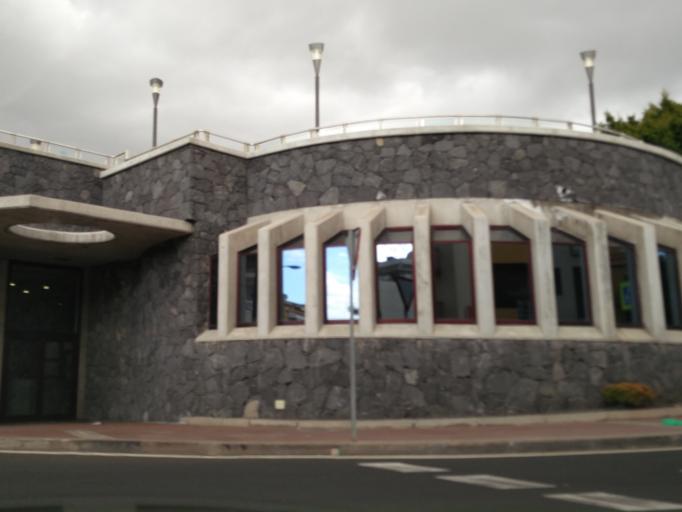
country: ES
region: Canary Islands
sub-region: Provincia de Santa Cruz de Tenerife
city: Arona
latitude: 28.0787
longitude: -16.6826
